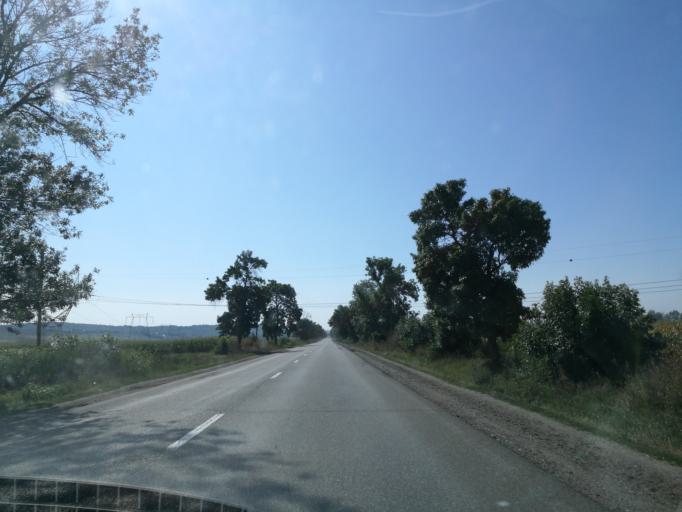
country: RO
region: Iasi
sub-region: Comuna Motca
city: Motca
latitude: 47.2257
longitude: 26.5993
